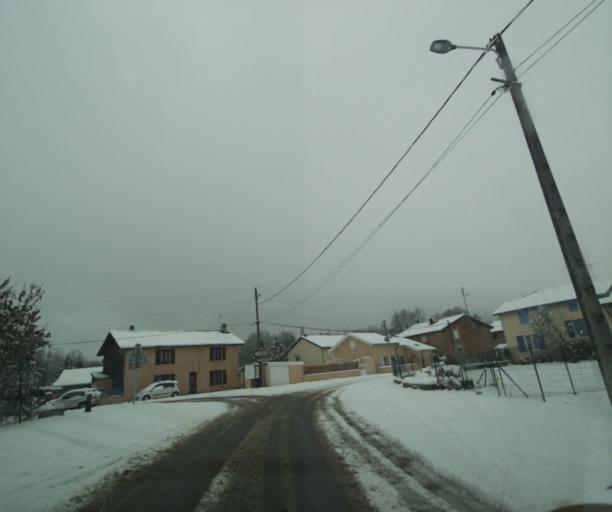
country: FR
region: Champagne-Ardenne
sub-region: Departement de la Haute-Marne
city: Wassy
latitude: 48.5623
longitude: 4.8960
